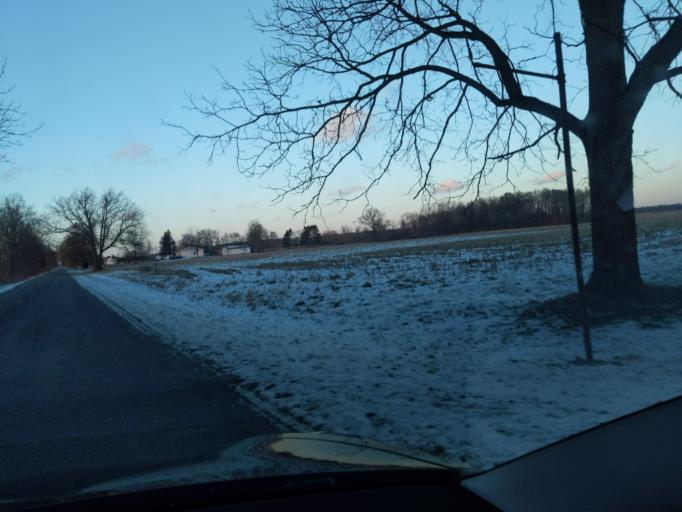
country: US
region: Michigan
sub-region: Ingham County
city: Stockbridge
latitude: 42.4547
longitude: -84.2778
